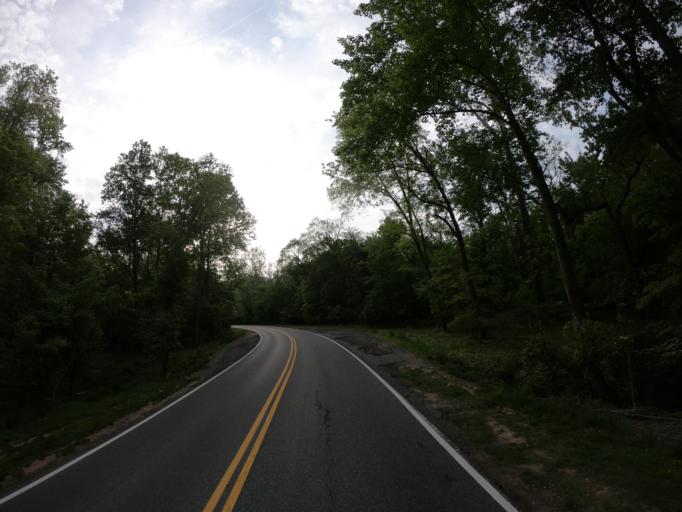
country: US
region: Maryland
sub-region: Montgomery County
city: South Kensington
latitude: 39.0260
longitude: -77.0961
